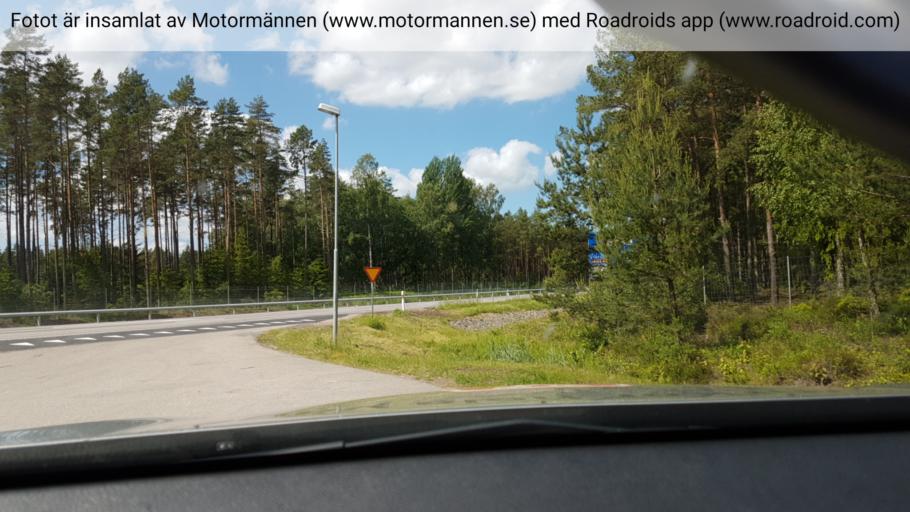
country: SE
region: Vaestra Goetaland
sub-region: Lidkopings Kommun
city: Lidkoping
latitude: 58.4857
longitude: 13.1923
